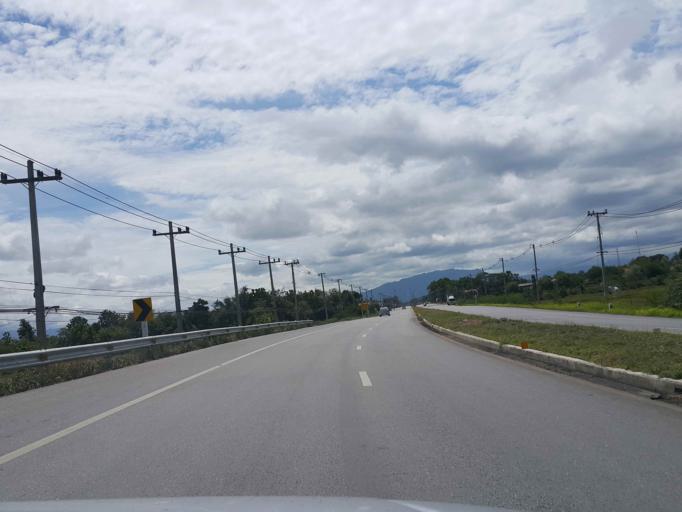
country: TH
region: Tak
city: Tak
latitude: 16.8849
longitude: 99.2038
